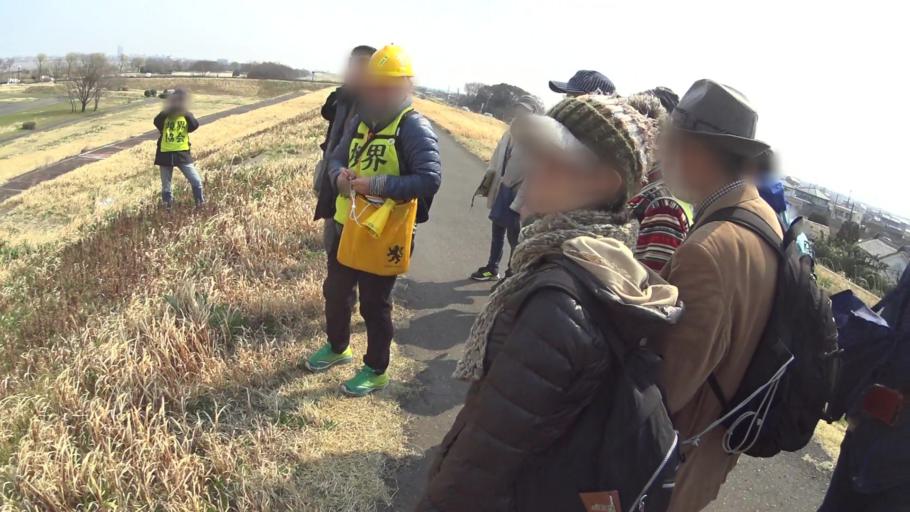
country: JP
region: Tochigi
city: Fujioka
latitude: 36.2092
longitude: 139.6653
